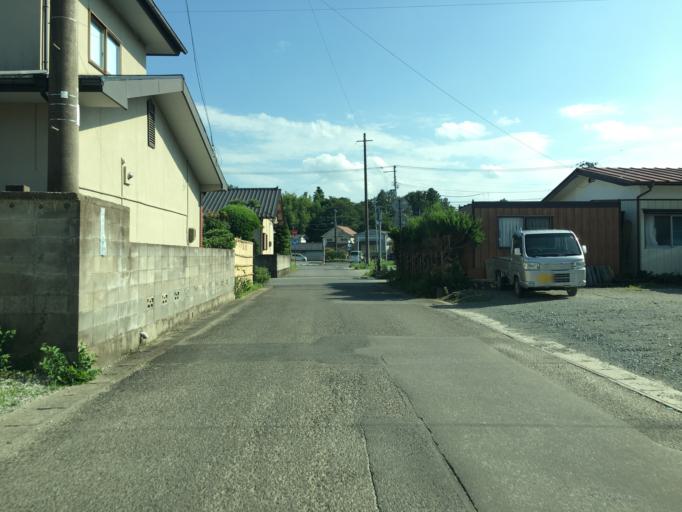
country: JP
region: Miyagi
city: Marumori
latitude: 37.8028
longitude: 140.9133
